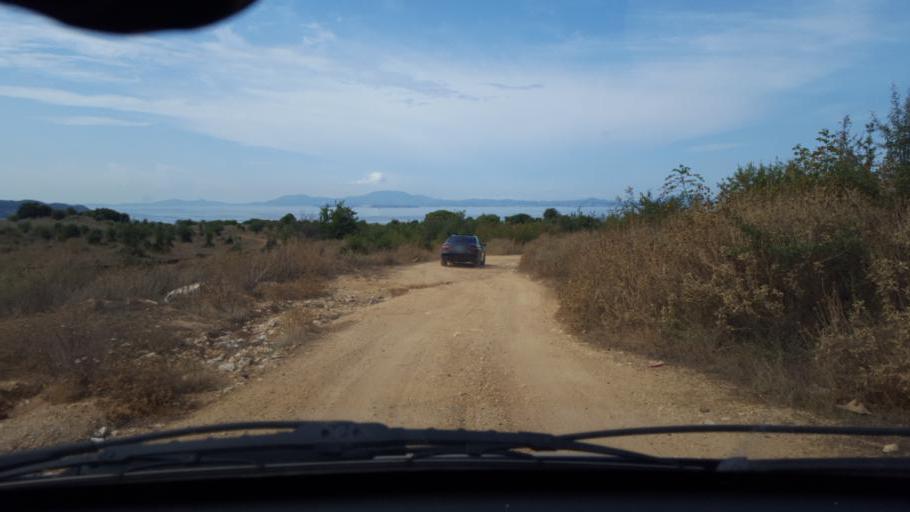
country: AL
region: Vlore
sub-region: Rrethi i Sarandes
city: Xarre
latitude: 39.7526
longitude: 19.9798
